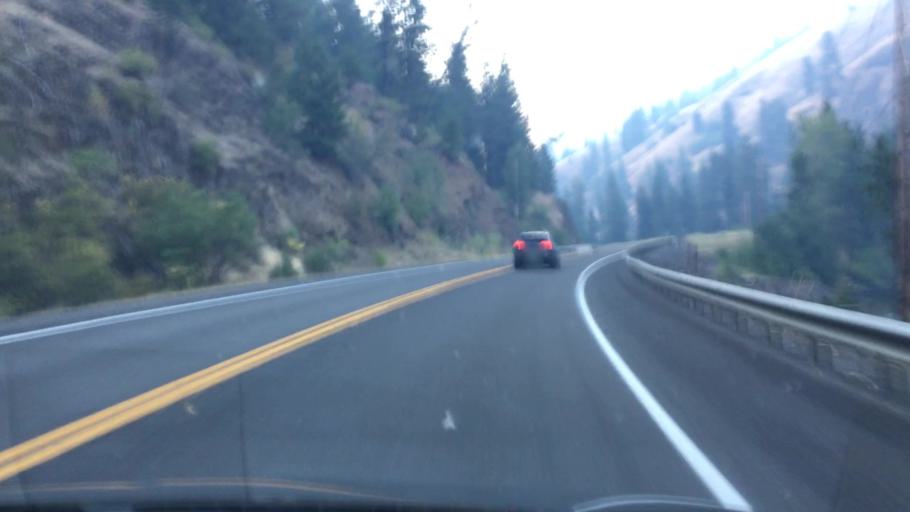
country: US
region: Idaho
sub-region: Valley County
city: McCall
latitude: 45.2243
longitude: -116.3218
